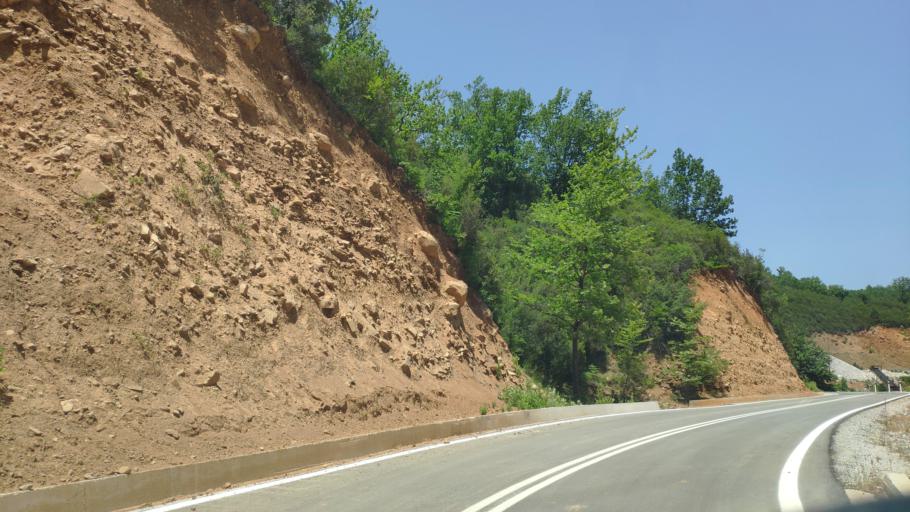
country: GR
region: Epirus
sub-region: Nomos Artas
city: Ano Kalentini
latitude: 39.1886
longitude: 21.3496
